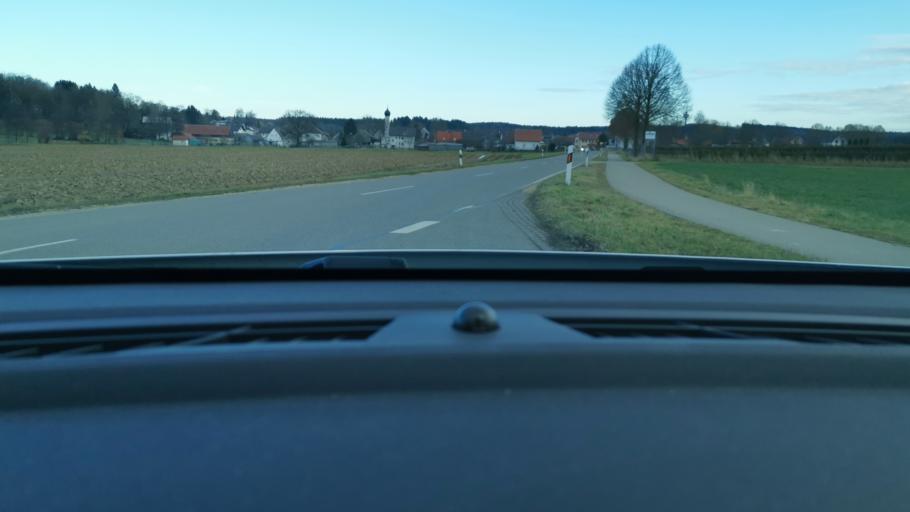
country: DE
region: Bavaria
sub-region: Swabia
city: Affing
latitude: 48.4991
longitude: 10.9928
